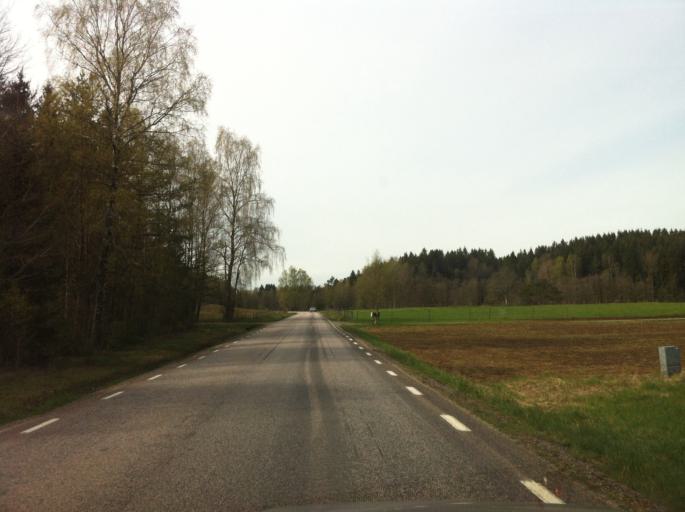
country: SE
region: Vaestra Goetaland
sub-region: Bollebygds Kommun
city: Bollebygd
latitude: 57.5849
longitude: 12.5732
